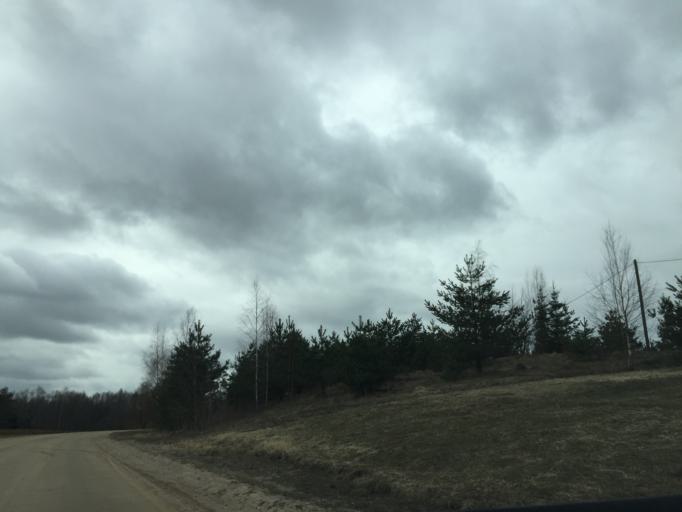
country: LV
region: Kraslavas Rajons
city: Kraslava
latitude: 55.9604
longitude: 27.0532
